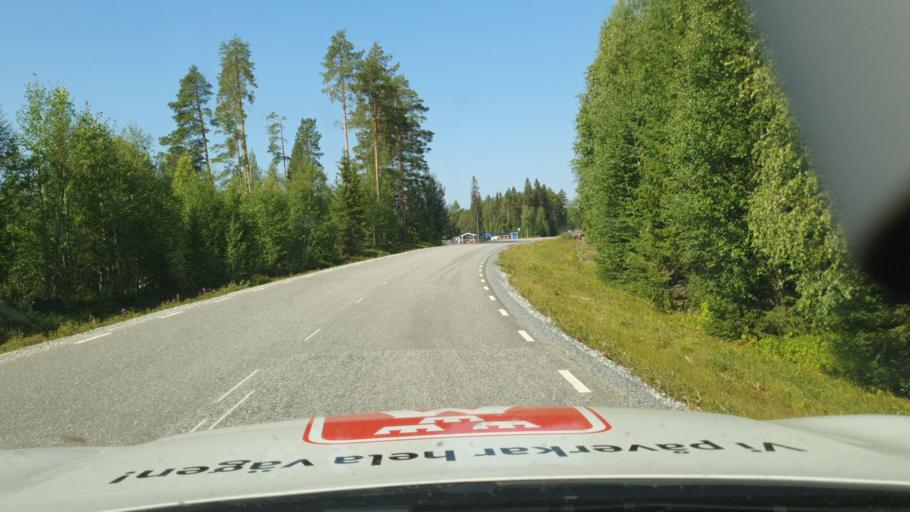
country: SE
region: Vaesterbotten
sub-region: Dorotea Kommun
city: Dorotea
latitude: 64.3583
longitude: 16.2132
